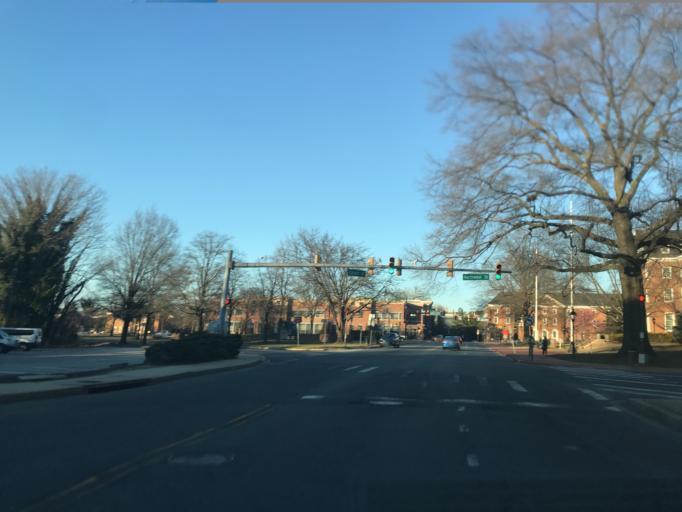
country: US
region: Maryland
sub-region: Anne Arundel County
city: Annapolis
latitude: 38.9798
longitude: -76.4953
